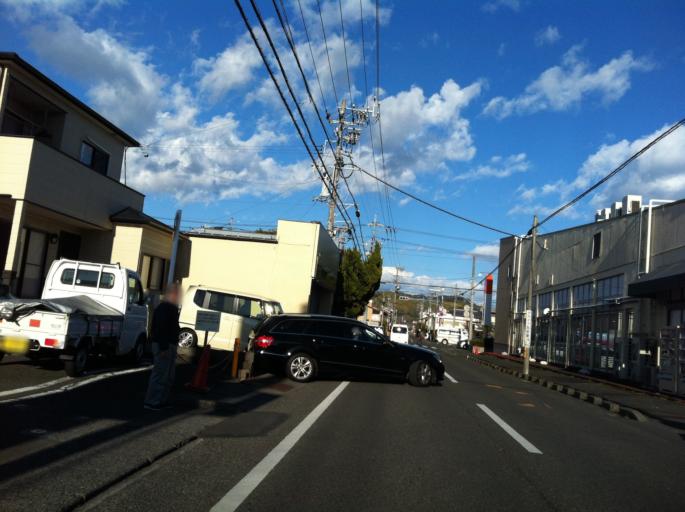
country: JP
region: Shizuoka
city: Shizuoka-shi
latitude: 35.0018
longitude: 138.3906
